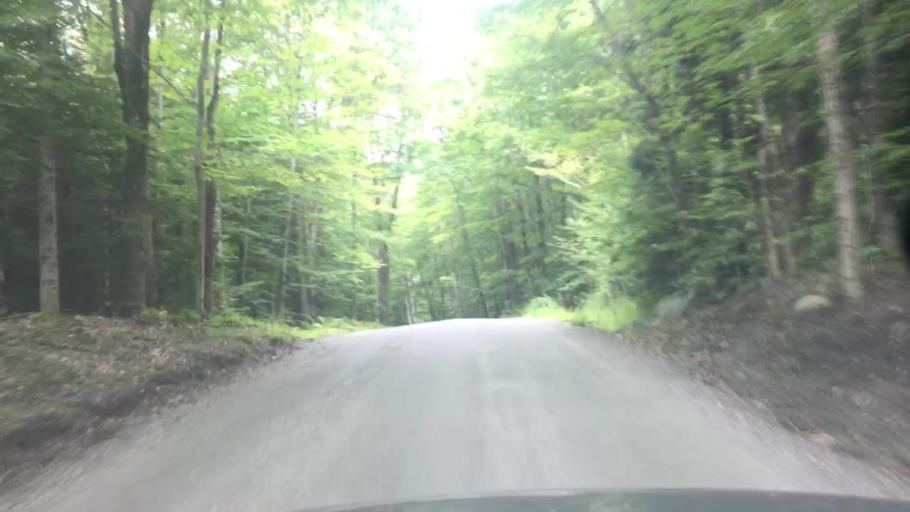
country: US
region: Vermont
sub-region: Windham County
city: Dover
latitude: 42.8212
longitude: -72.7734
